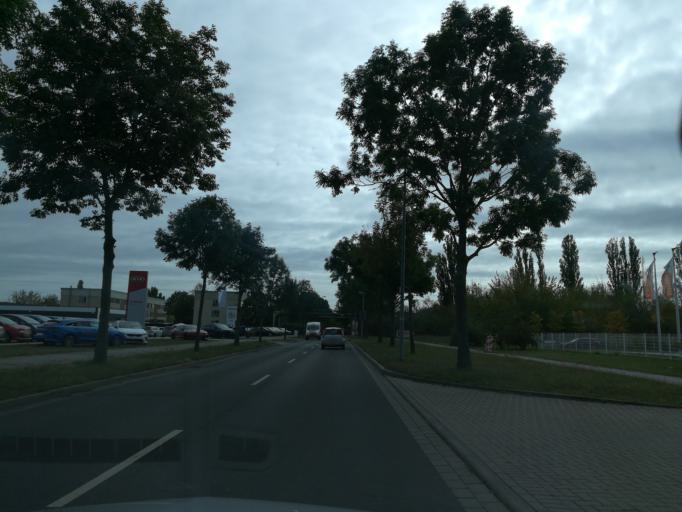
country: DE
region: Saxony-Anhalt
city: Neue Neustadt
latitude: 52.1642
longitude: 11.6078
